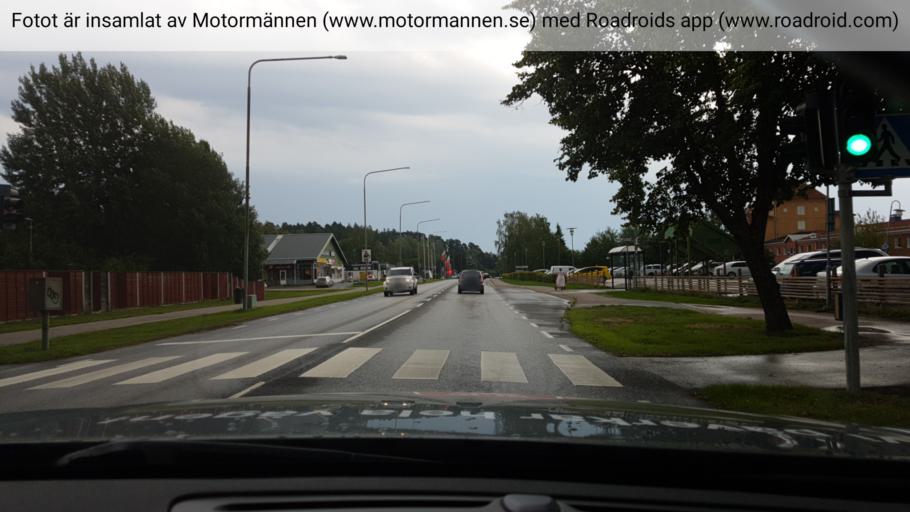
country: SE
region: Uppsala
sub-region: Habo Kommun
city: Balsta
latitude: 59.5664
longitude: 17.5338
